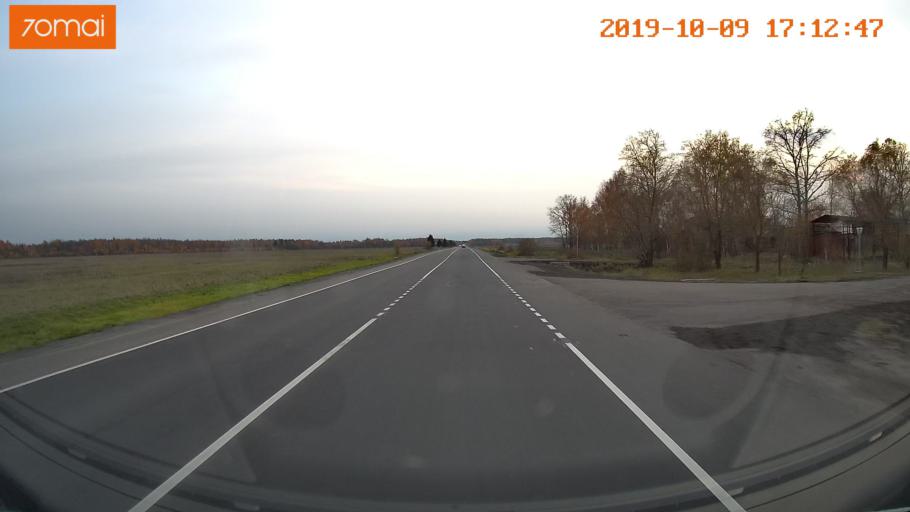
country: RU
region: Ivanovo
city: Privolzhsk
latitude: 57.3239
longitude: 41.2357
